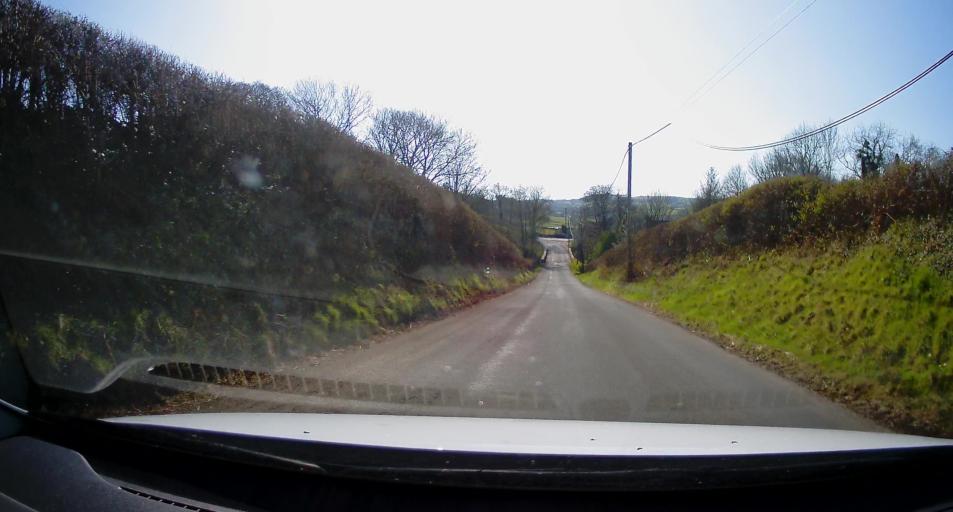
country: GB
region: Wales
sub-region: County of Ceredigion
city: Penparcau
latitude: 52.3490
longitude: -4.0646
